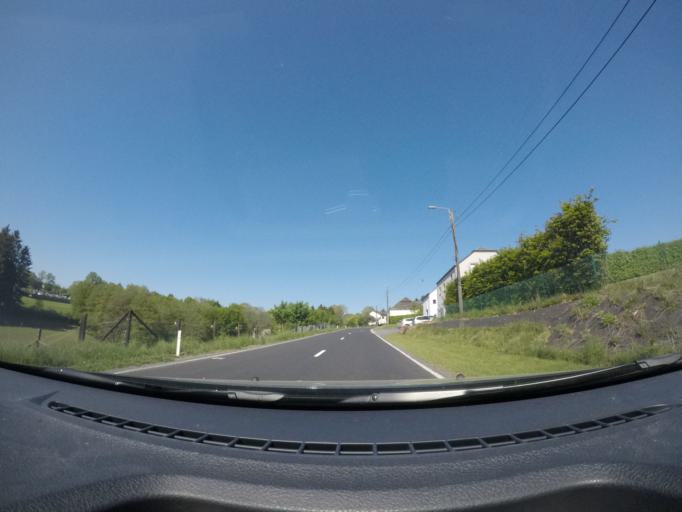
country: BE
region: Wallonia
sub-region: Province du Luxembourg
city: Fauvillers
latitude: 49.8520
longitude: 5.6716
